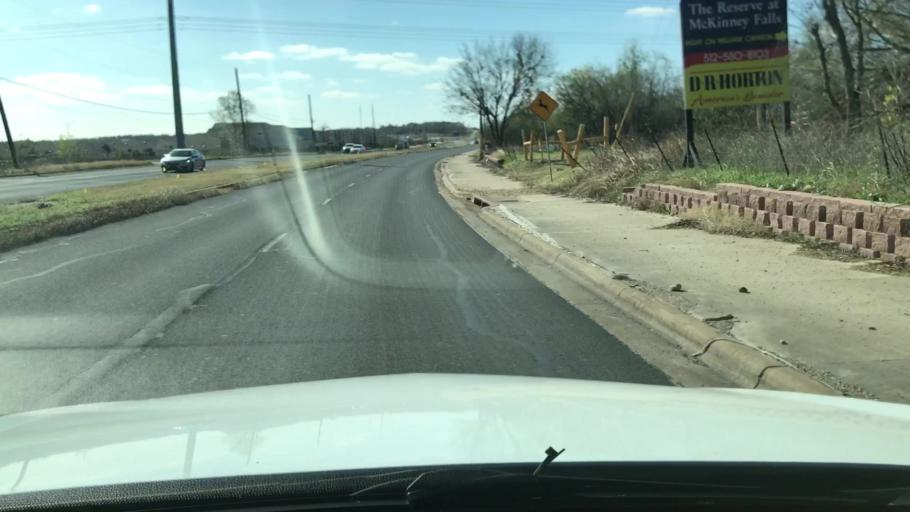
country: US
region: Texas
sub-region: Travis County
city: Onion Creek
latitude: 30.1673
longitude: -97.7234
